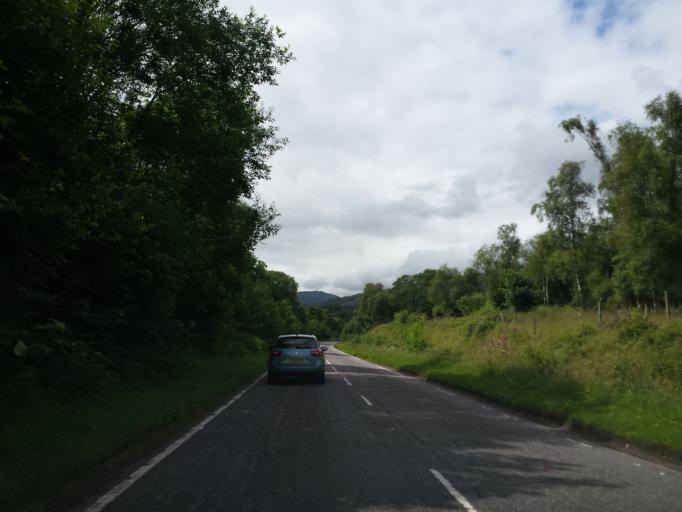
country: GB
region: Scotland
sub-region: Highland
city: Fort William
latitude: 56.8504
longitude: -5.1685
